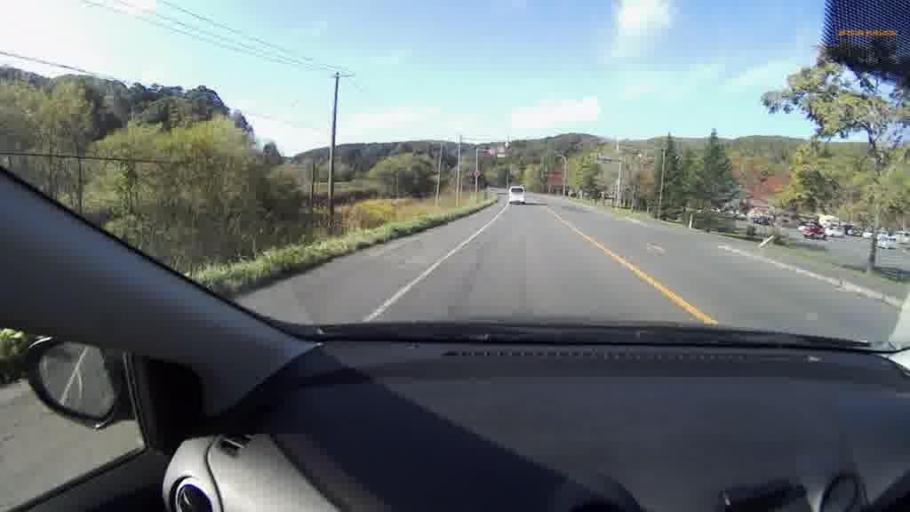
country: JP
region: Hokkaido
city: Kushiro
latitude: 42.9943
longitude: 144.4630
